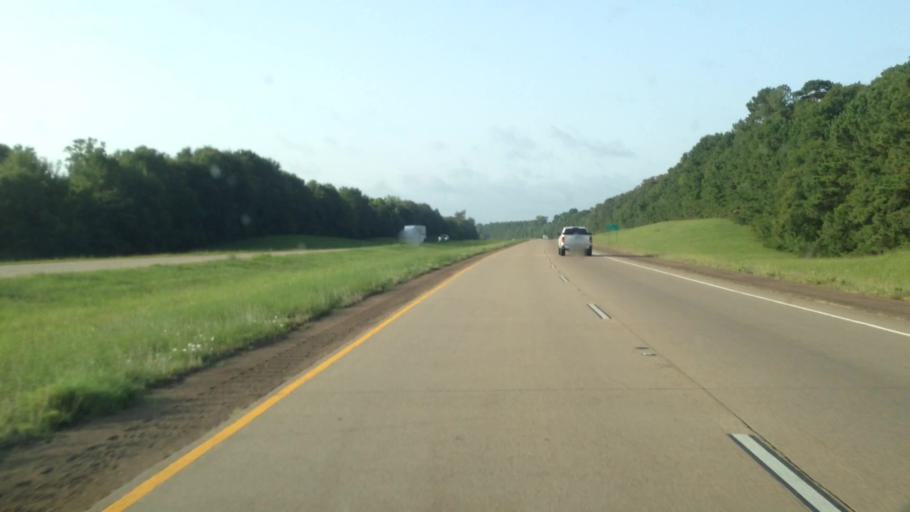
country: US
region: Louisiana
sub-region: Rapides Parish
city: Woodworth
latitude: 31.1517
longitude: -92.4538
